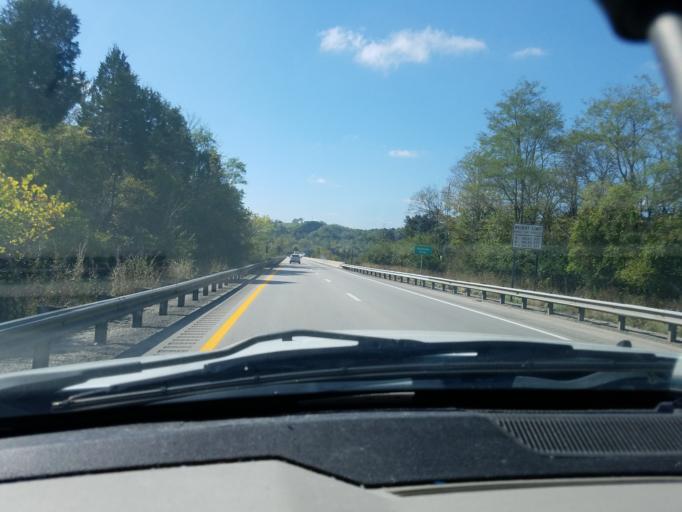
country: US
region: Kentucky
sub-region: Franklin County
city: Frankfort
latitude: 38.1625
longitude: -84.8500
